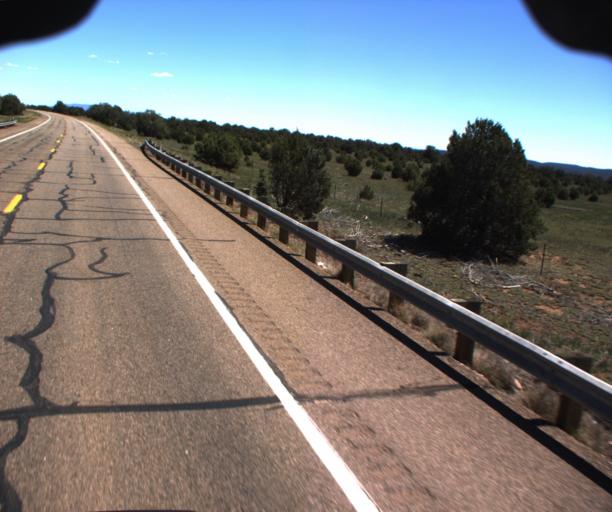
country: US
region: Arizona
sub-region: Yavapai County
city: Paulden
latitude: 35.0991
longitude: -112.4233
